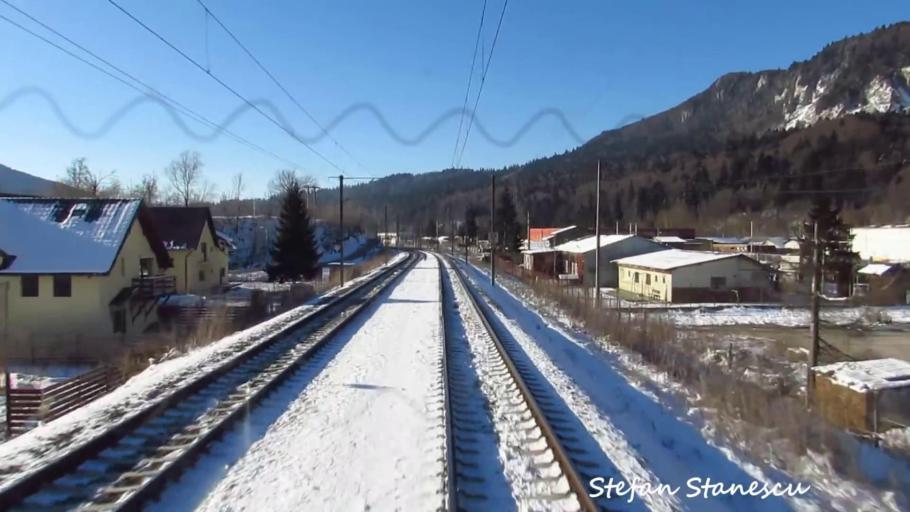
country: RO
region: Prahova
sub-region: Oras Busteni
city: Poiana Tapului
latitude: 45.3811
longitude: 25.5409
